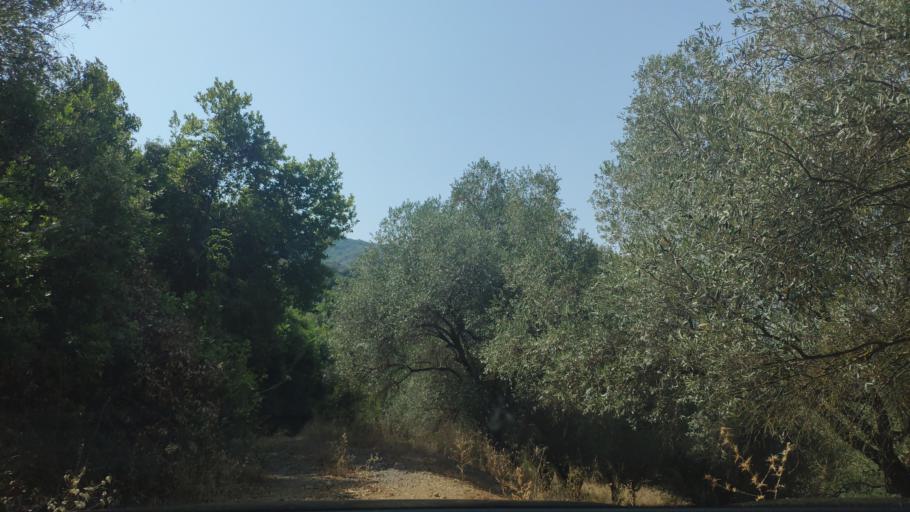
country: GR
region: West Greece
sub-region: Nomos Aitolias kai Akarnanias
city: Fitiai
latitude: 38.7342
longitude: 21.1817
